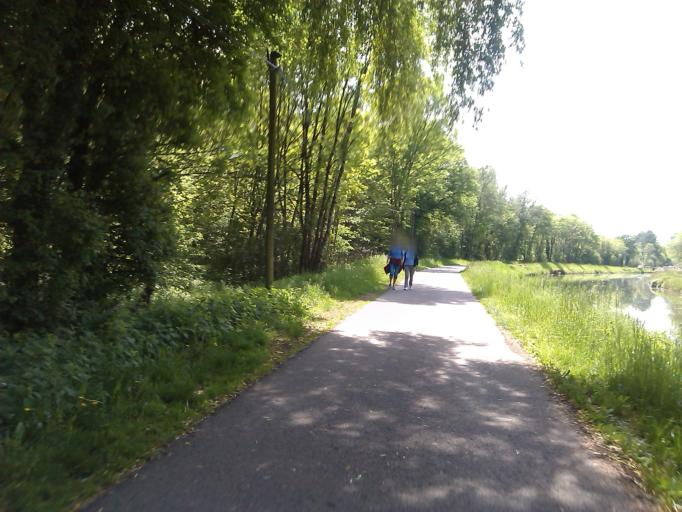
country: FR
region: Franche-Comte
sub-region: Departement du Doubs
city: Avanne-Aveney
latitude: 47.1831
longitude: 5.9570
